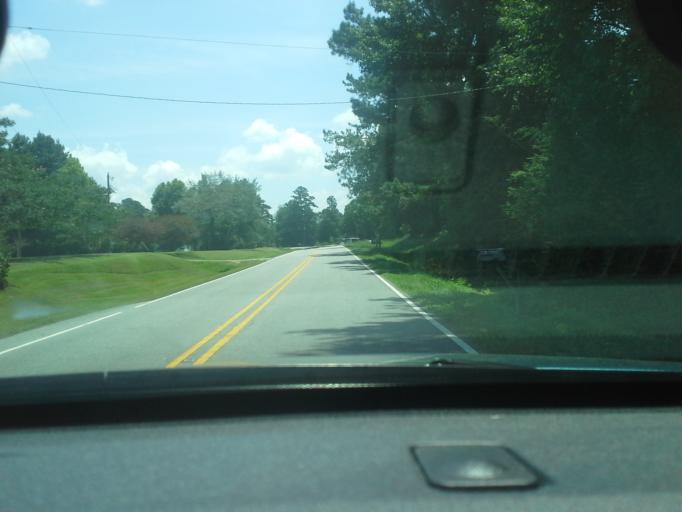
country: US
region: North Carolina
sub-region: Chowan County
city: Edenton
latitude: 35.9273
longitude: -76.6016
